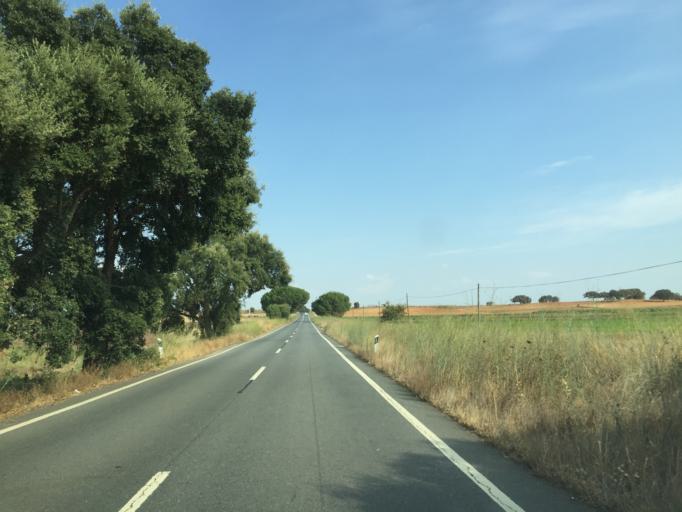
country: PT
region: Beja
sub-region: Aljustrel
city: Aljustrel
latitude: 37.9324
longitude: -8.3497
